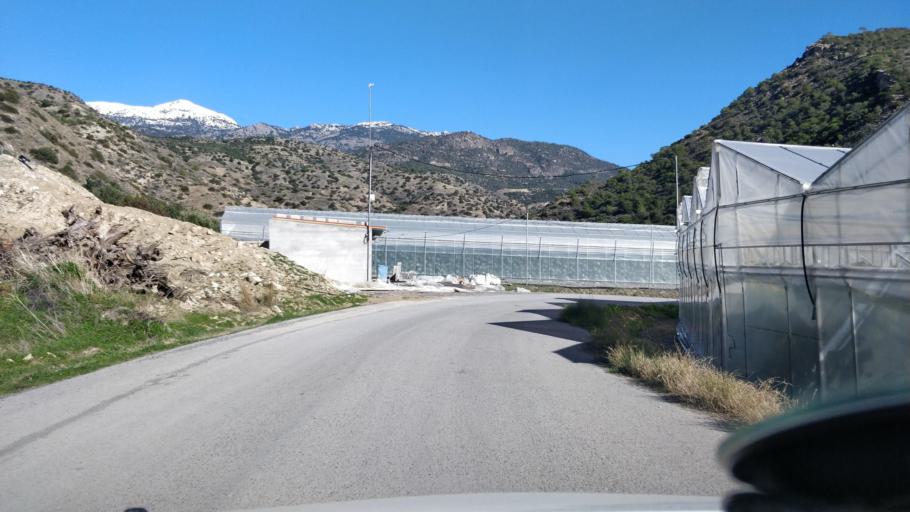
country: GR
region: Crete
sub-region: Nomos Lasithiou
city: Gra Liyia
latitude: 34.9905
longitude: 25.4830
